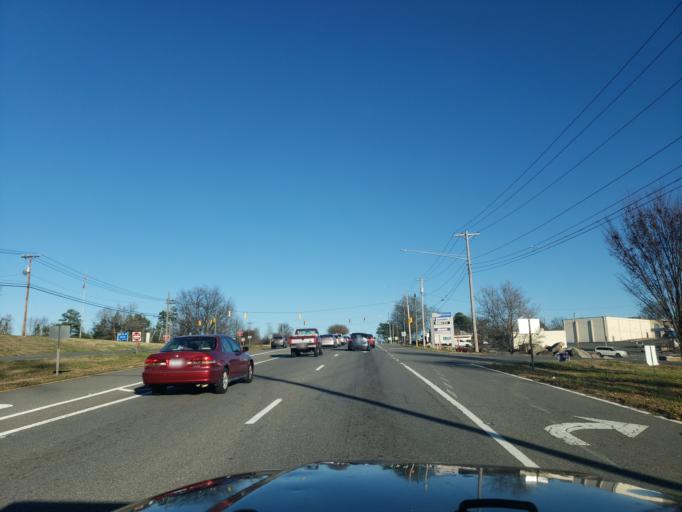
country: US
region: North Carolina
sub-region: Gaston County
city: Gastonia
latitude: 35.2586
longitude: -81.2292
